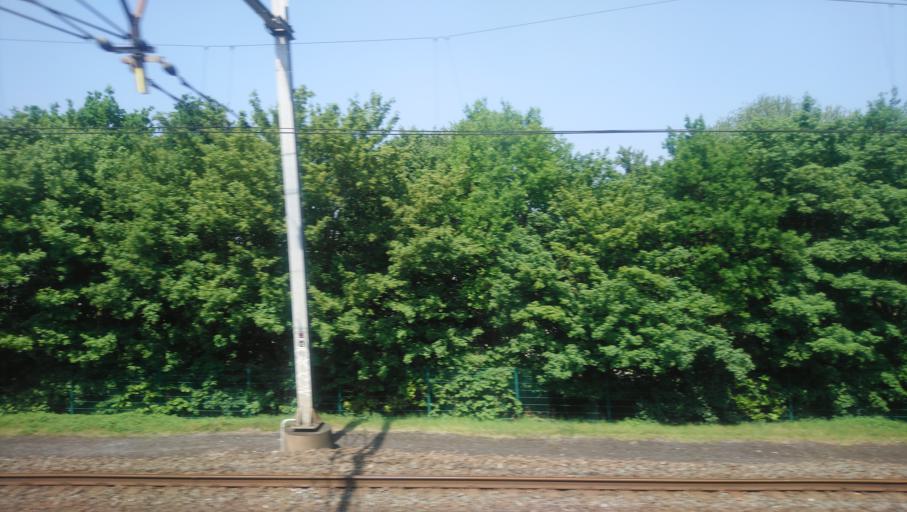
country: NL
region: North Holland
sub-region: Gemeente Amsterdam
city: Amsterdam
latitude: 52.3891
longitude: 4.8589
